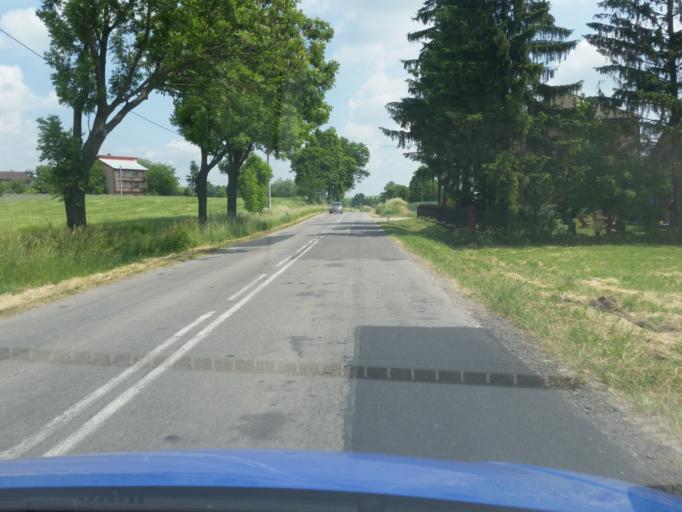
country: PL
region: Swietokrzyskie
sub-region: Powiat pinczowski
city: Dzialoszyce
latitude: 50.3279
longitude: 20.3246
